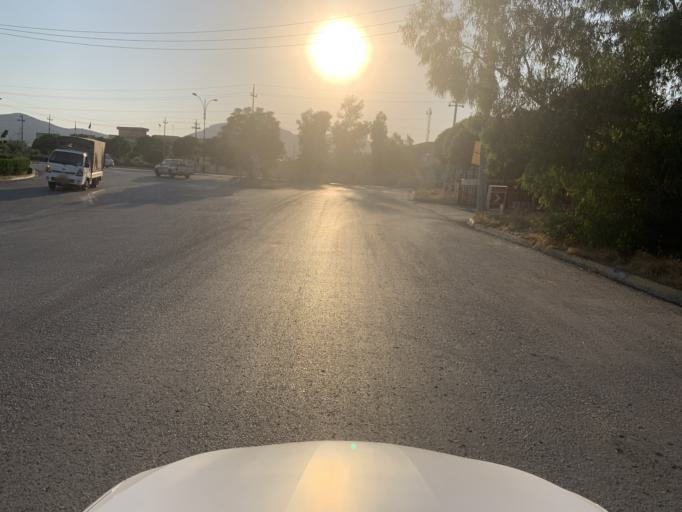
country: IQ
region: As Sulaymaniyah
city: Raniye
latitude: 36.2459
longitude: 44.8826
